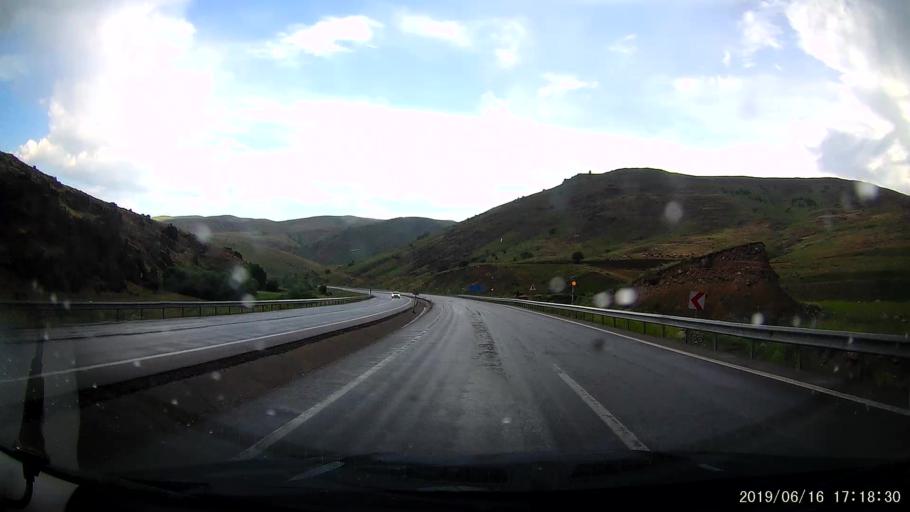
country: TR
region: Erzincan
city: Tercan
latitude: 39.8133
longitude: 40.5287
